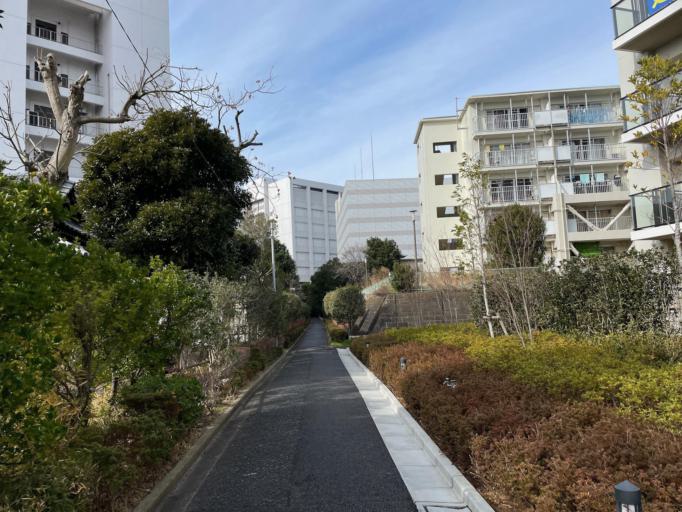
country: JP
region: Tokyo
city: Urayasu
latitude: 35.6806
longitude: 139.8586
